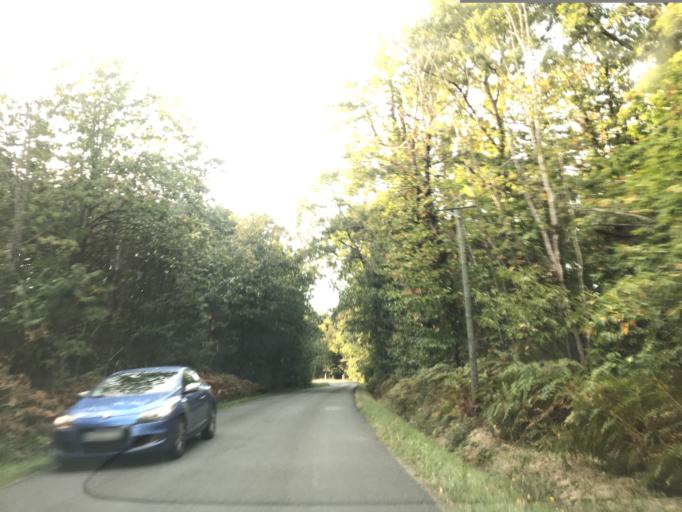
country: FR
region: Aquitaine
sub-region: Departement de la Dordogne
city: Riberac
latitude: 45.2034
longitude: 0.3507
